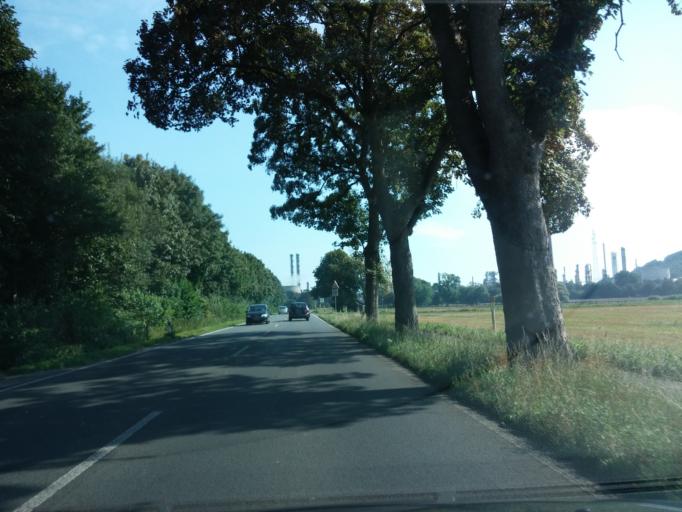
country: DE
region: North Rhine-Westphalia
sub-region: Regierungsbezirk Munster
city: Gladbeck
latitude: 51.6166
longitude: 7.0192
